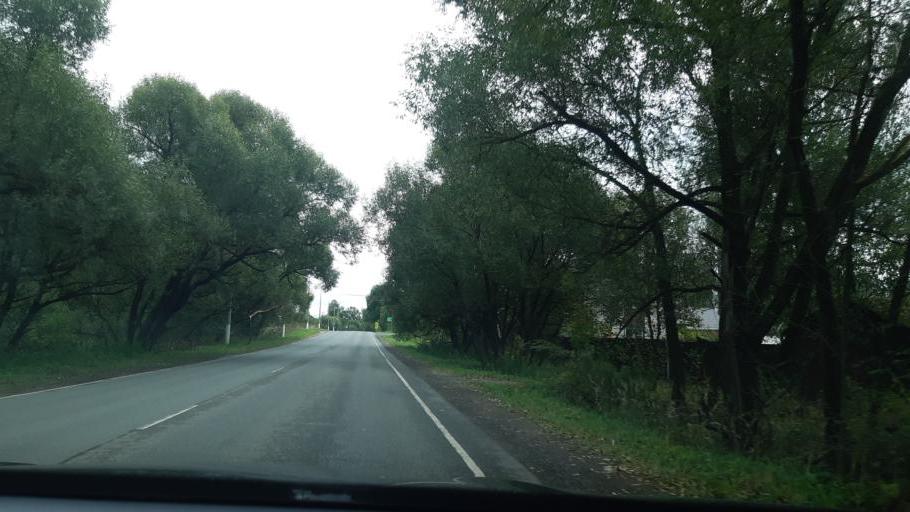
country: RU
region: Moskovskaya
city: Melikhovo
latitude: 55.1150
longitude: 37.6418
